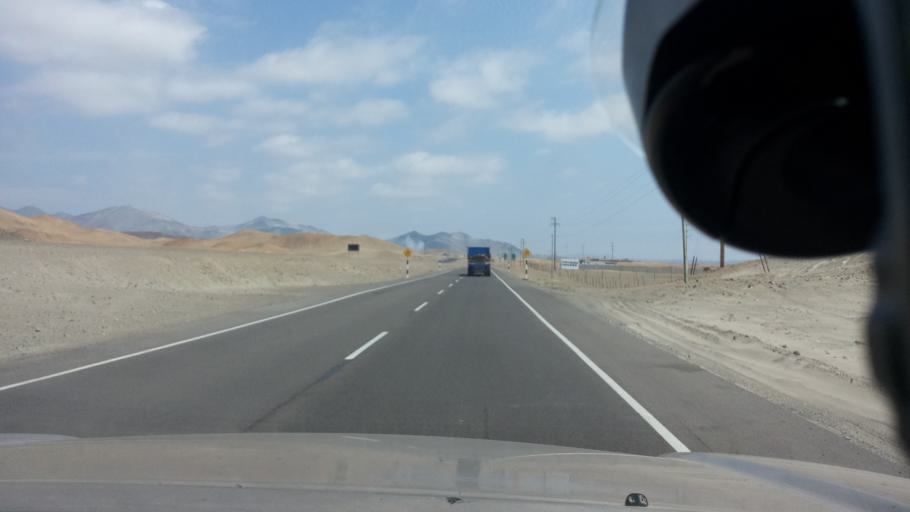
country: PE
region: Ancash
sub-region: Provincia de Huarmey
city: Huarmey
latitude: -10.0353
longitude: -78.1644
